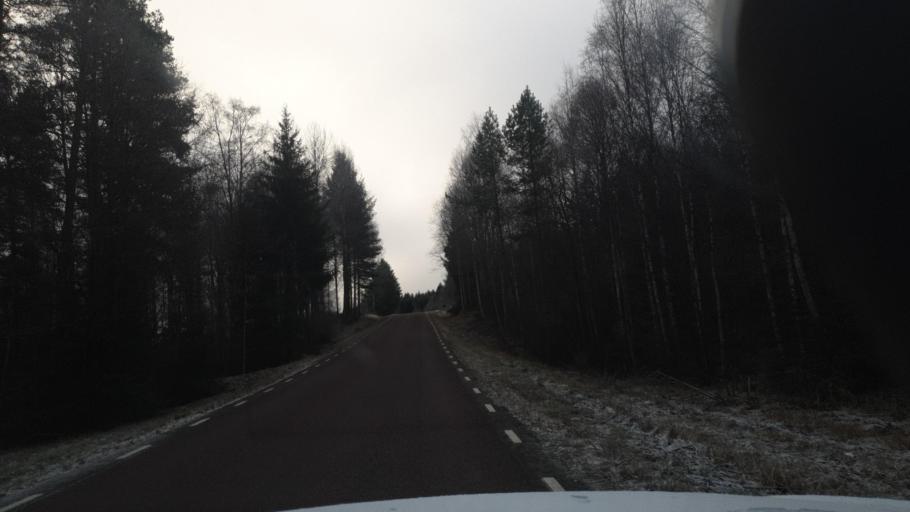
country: SE
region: Vaermland
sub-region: Karlstads Kommun
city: Edsvalla
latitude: 59.5168
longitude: 13.1110
